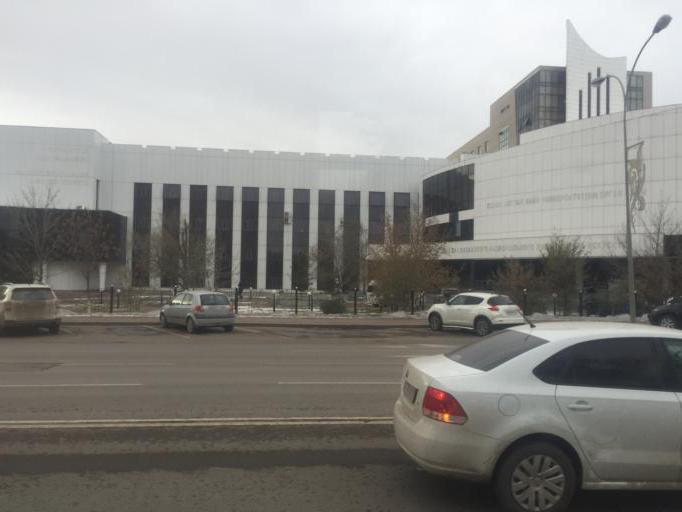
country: KZ
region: Astana Qalasy
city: Astana
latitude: 51.1736
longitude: 71.4117
